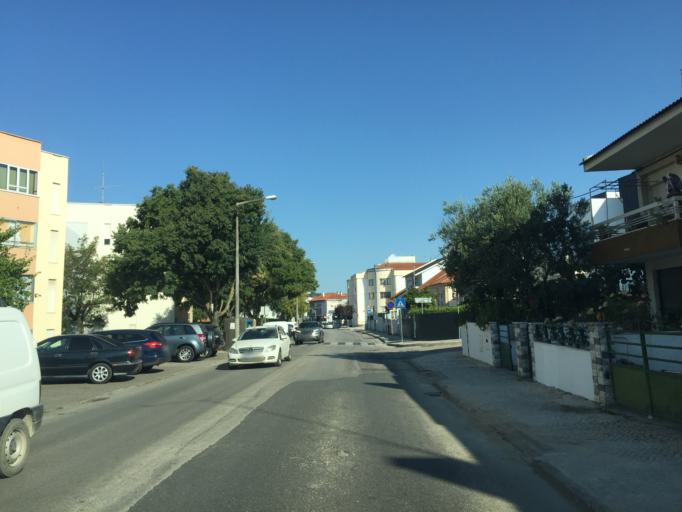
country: PT
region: Santarem
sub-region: Tomar
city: Tomar
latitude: 39.6032
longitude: -8.4004
